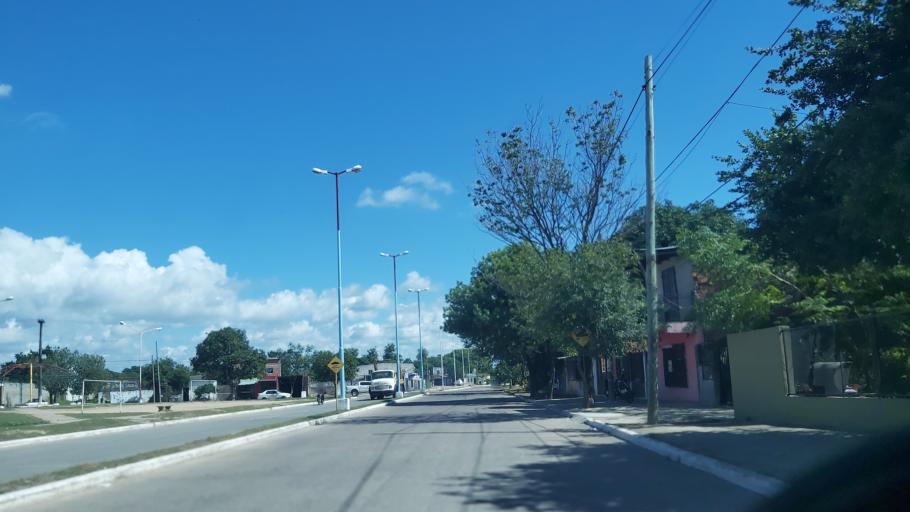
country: AR
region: Corrientes
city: Corrientes
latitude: -27.4833
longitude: -58.8487
